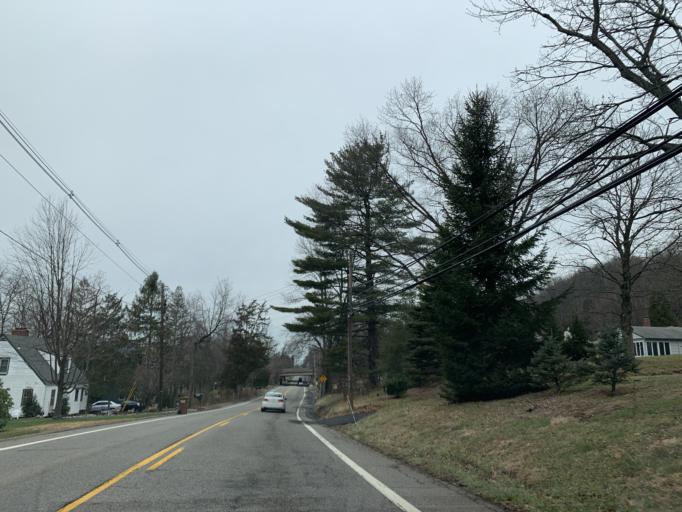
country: US
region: New Jersey
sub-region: Somerset County
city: Green Knoll
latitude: 40.6424
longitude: -74.6220
